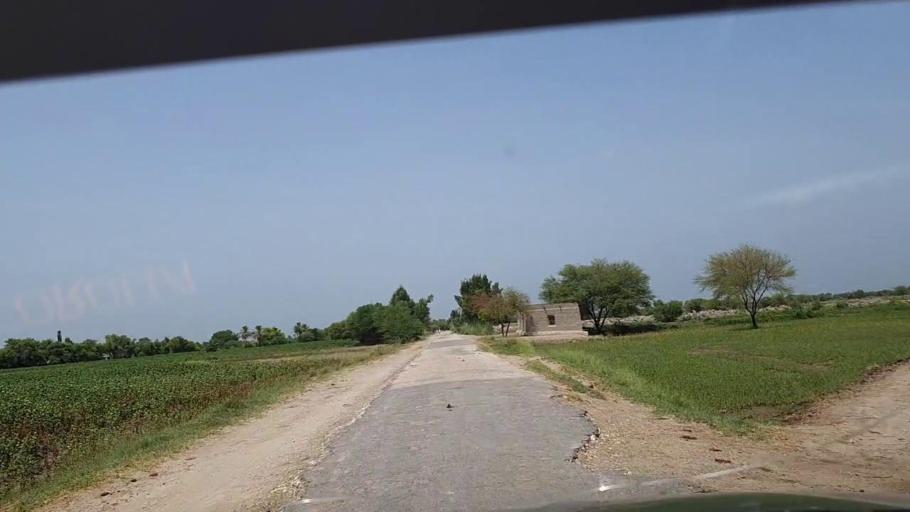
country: PK
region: Sindh
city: Khanpur
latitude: 27.8063
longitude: 69.4506
